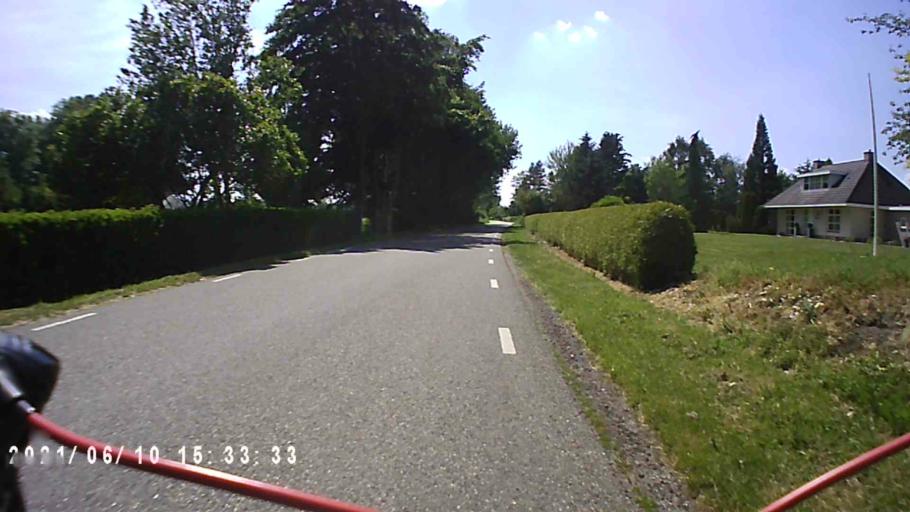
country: NL
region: Friesland
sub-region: Gemeente Achtkarspelen
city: Surhuisterveen
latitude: 53.1683
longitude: 6.1719
